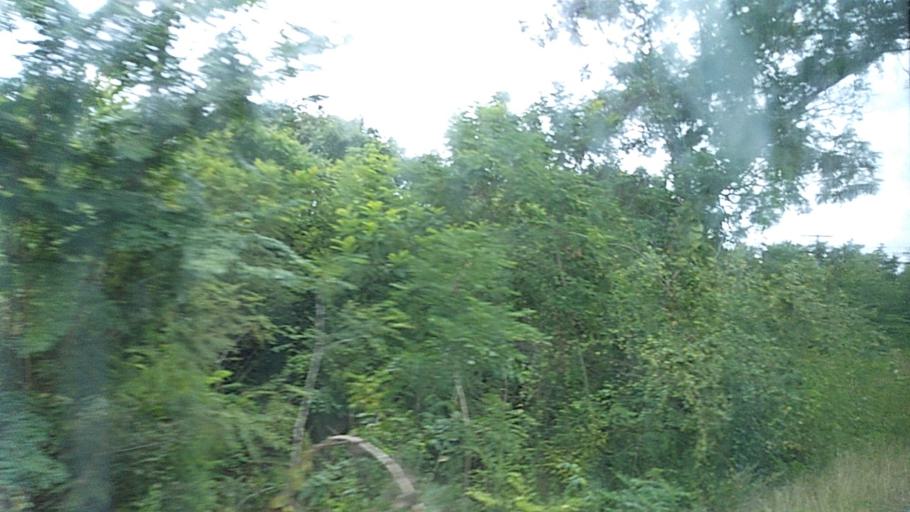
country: TH
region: Maha Sarakham
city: Kantharawichai
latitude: 16.3379
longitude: 103.2186
